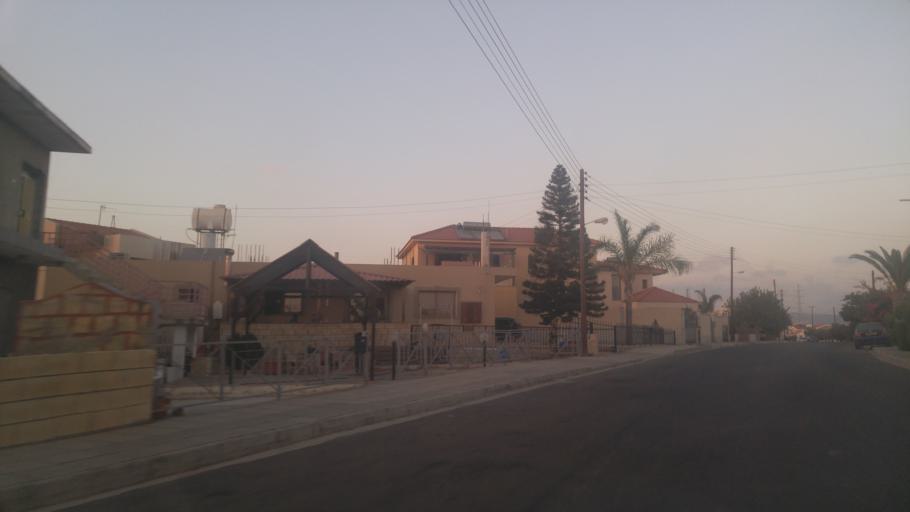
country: CY
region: Larnaka
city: Kolossi
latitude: 34.6604
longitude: 32.9565
